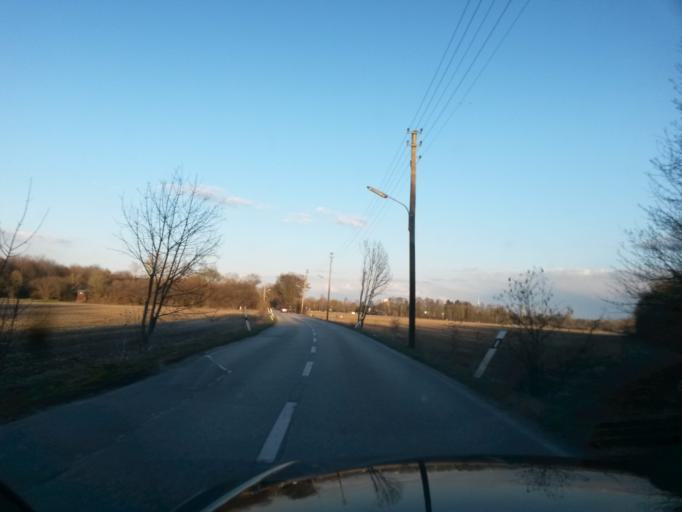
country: DE
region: Bavaria
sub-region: Upper Bavaria
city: Karlsfeld
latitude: 48.1979
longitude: 11.4720
